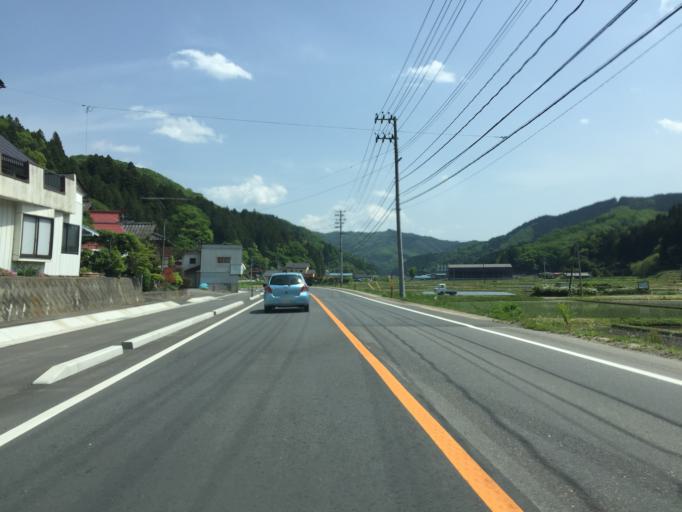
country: JP
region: Fukushima
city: Ishikawa
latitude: 37.0981
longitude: 140.5117
